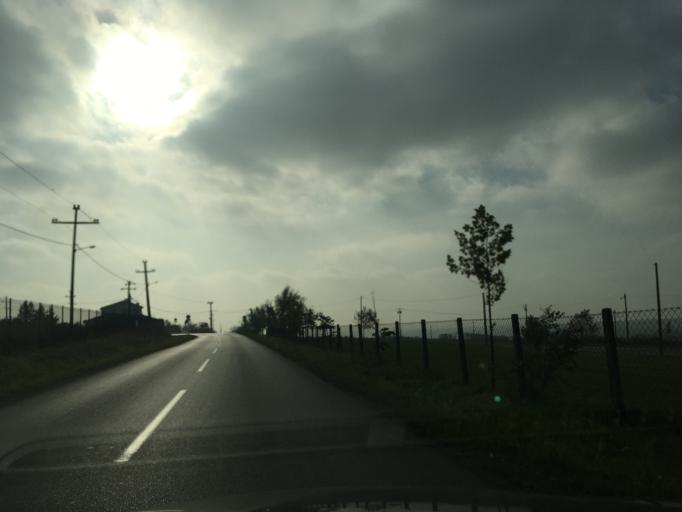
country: RS
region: Central Serbia
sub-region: Belgrade
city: Sopot
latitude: 44.4834
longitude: 20.5583
